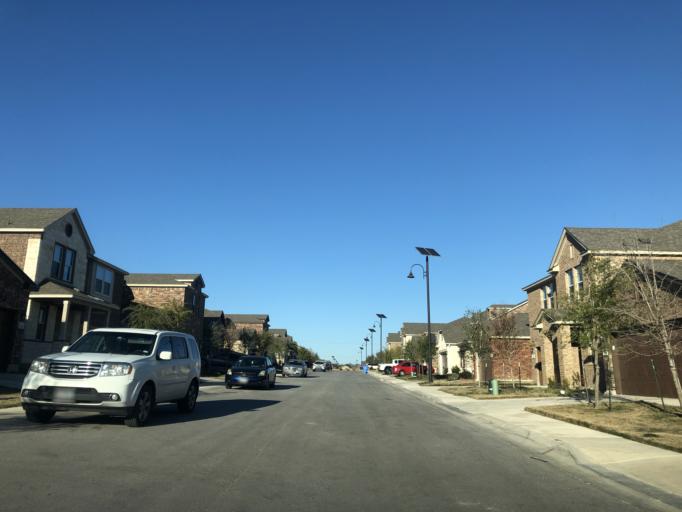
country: US
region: Texas
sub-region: Travis County
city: Windemere
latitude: 30.4717
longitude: -97.6575
